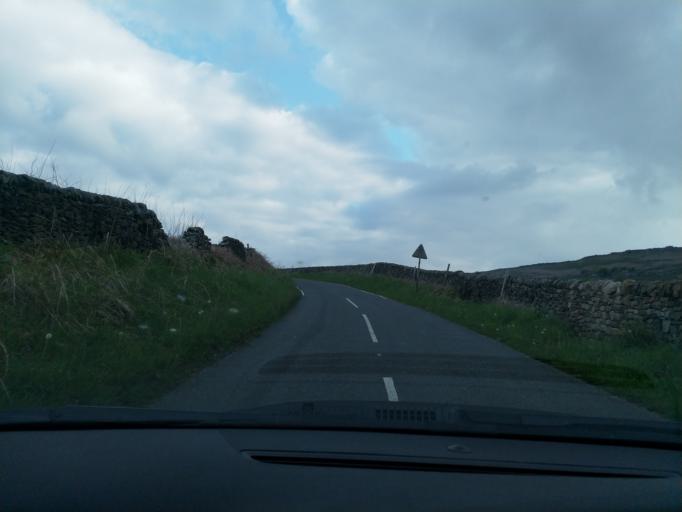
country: GB
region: England
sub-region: Derbyshire
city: Hathersage
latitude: 53.3335
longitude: -1.6299
